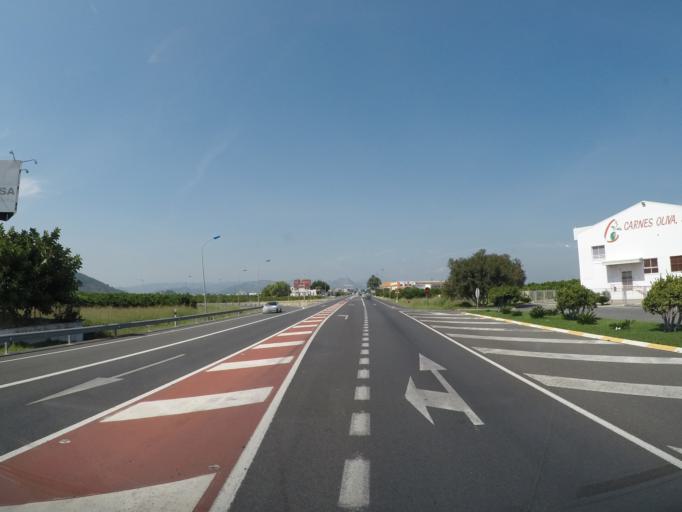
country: ES
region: Valencia
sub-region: Provincia de Valencia
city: Piles
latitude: 38.9288
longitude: -0.1332
